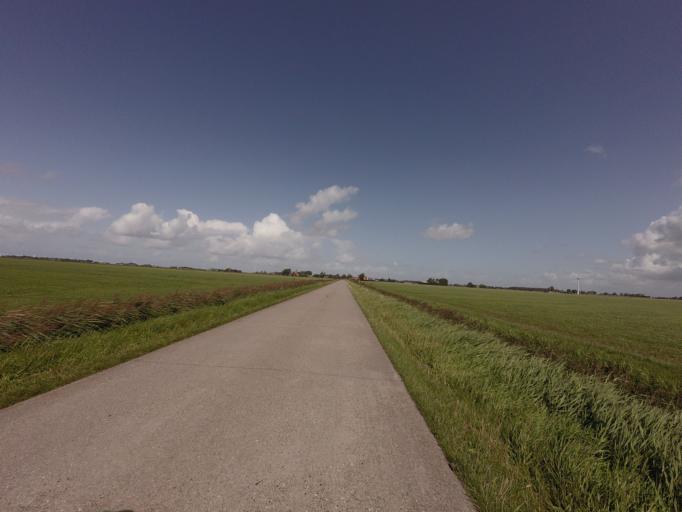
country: NL
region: Friesland
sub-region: Sudwest Fryslan
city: Makkum
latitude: 53.0709
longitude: 5.4541
